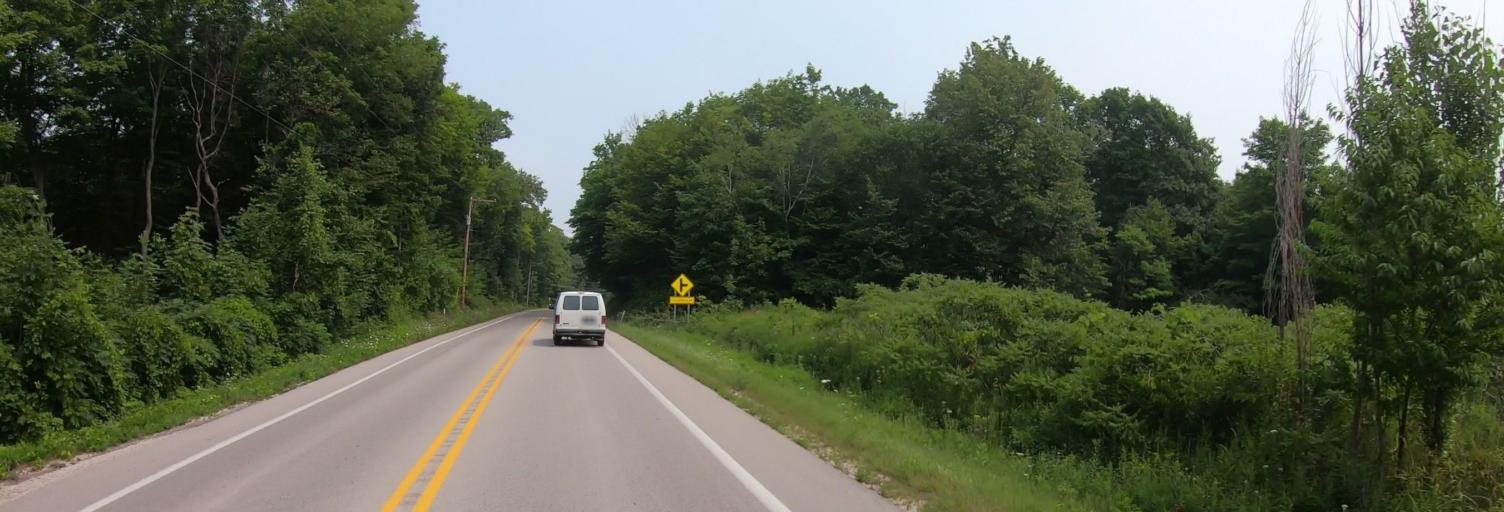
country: US
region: Michigan
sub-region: Leelanau County
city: Leland
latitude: 44.9781
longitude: -85.7779
